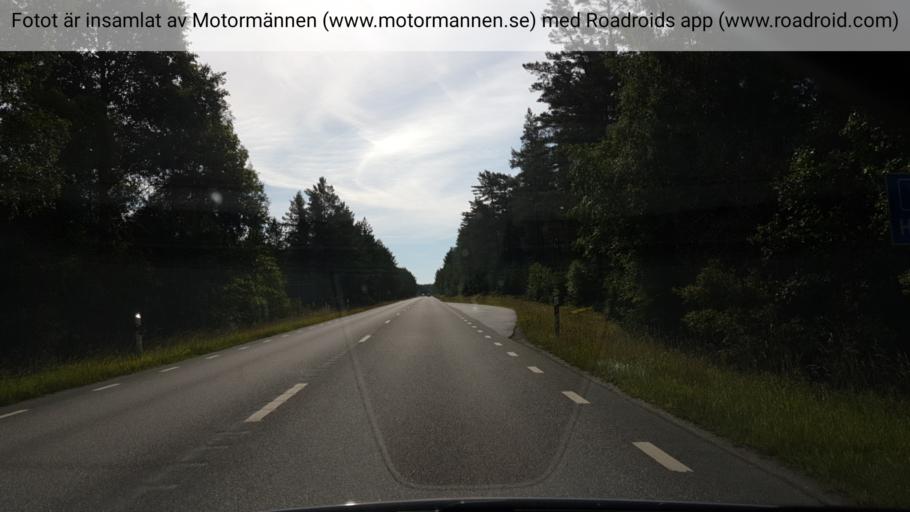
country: SE
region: Vaestra Goetaland
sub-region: Hjo Kommun
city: Hjo
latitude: 58.3391
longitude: 14.2308
